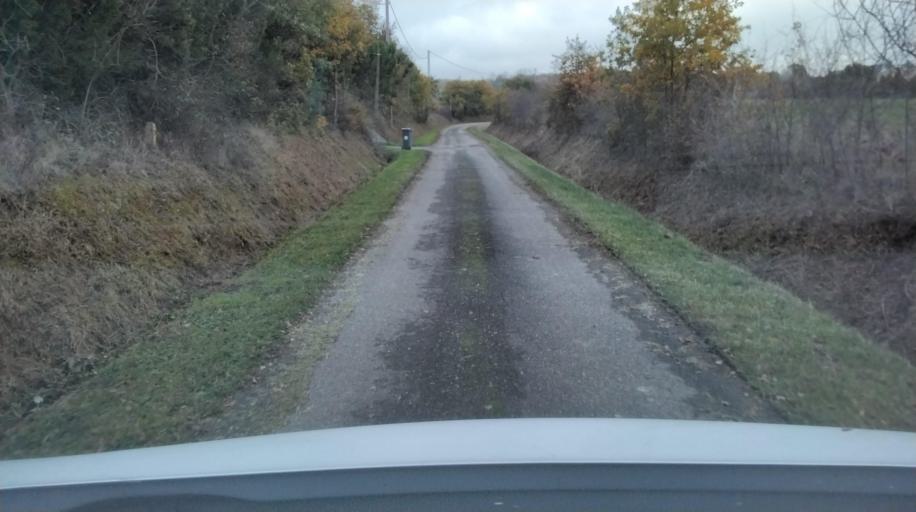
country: FR
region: Midi-Pyrenees
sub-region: Departement de la Haute-Garonne
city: Le Fousseret
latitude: 43.2714
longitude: 1.0302
